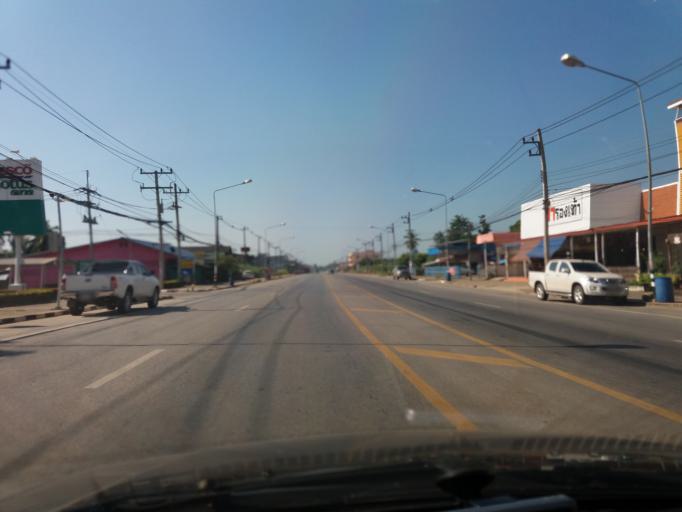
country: TH
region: Kamphaeng Phet
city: Khlong Khlung
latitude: 16.2300
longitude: 99.7329
